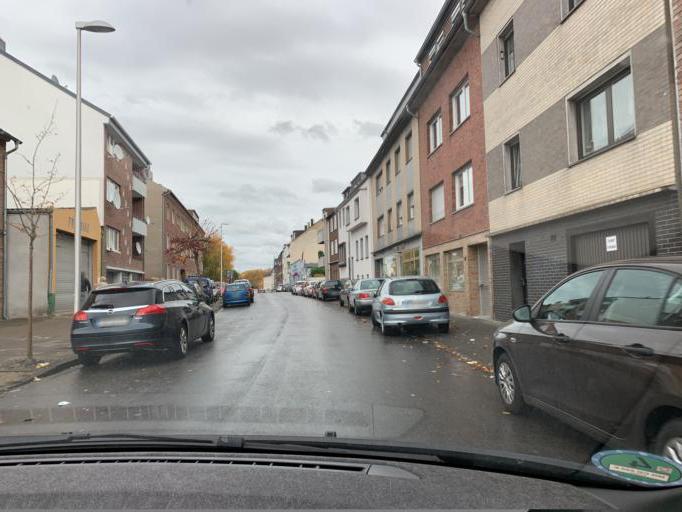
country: DE
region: North Rhine-Westphalia
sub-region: Regierungsbezirk Koln
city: Dueren
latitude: 50.8053
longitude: 6.4962
